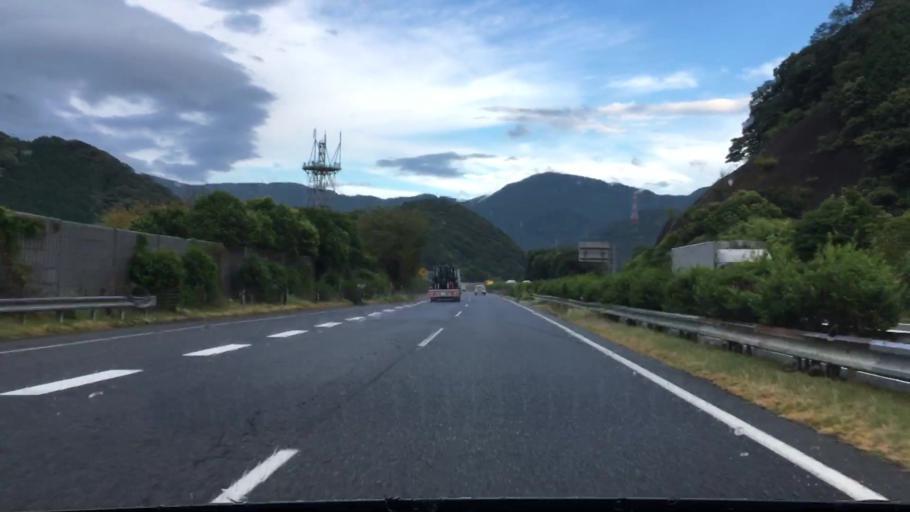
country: JP
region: Fukuoka
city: Kitakyushu
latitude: 33.8024
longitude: 130.8563
